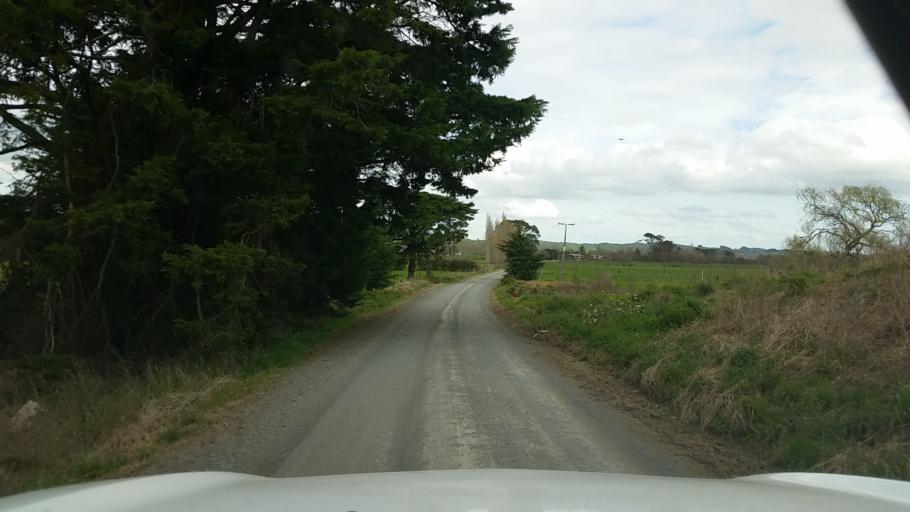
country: NZ
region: Waikato
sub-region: Hauraki District
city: Ngatea
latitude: -37.5061
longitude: 175.4411
